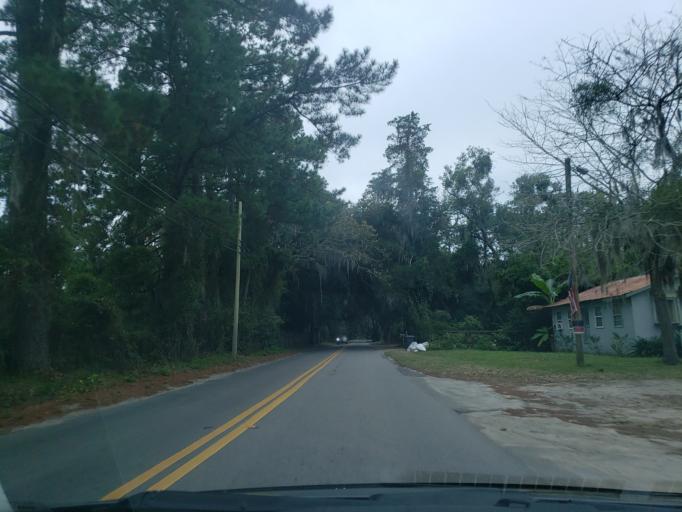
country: US
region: Georgia
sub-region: Chatham County
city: Montgomery
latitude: 31.9575
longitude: -81.1038
